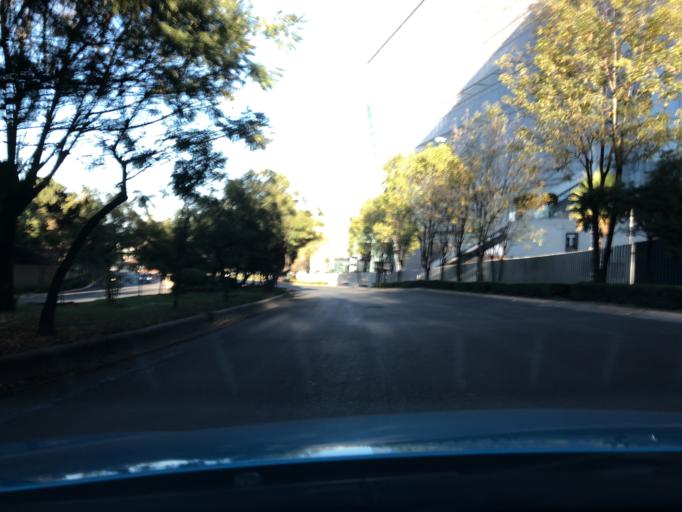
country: MX
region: Mexico City
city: Col. Bosques de las Lomas
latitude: 19.3661
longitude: -99.2656
